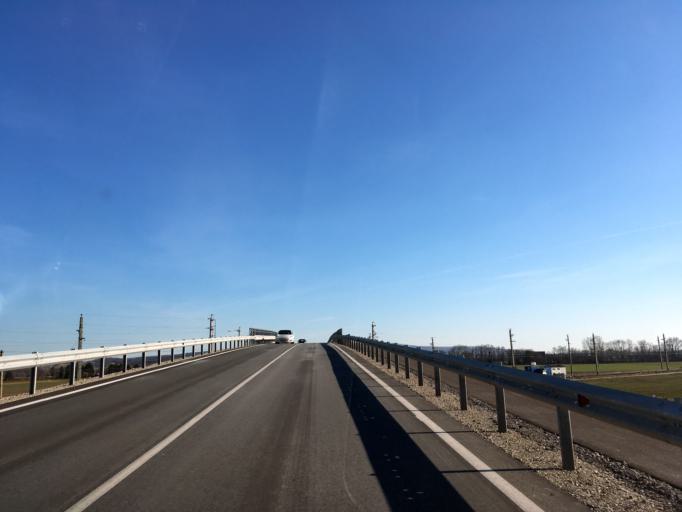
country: AT
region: Lower Austria
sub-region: Politischer Bezirk Baden
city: Ebreichsdorf
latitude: 47.9361
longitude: 16.4182
